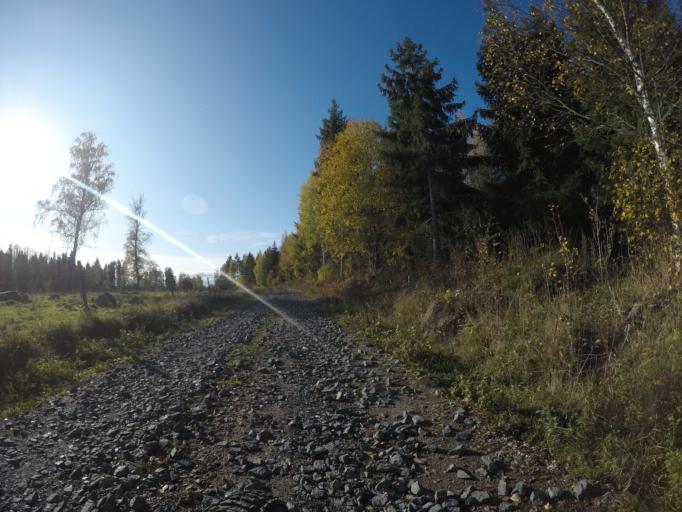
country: SE
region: Vaestmanland
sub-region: Kungsors Kommun
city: Kungsoer
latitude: 59.3231
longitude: 16.0911
